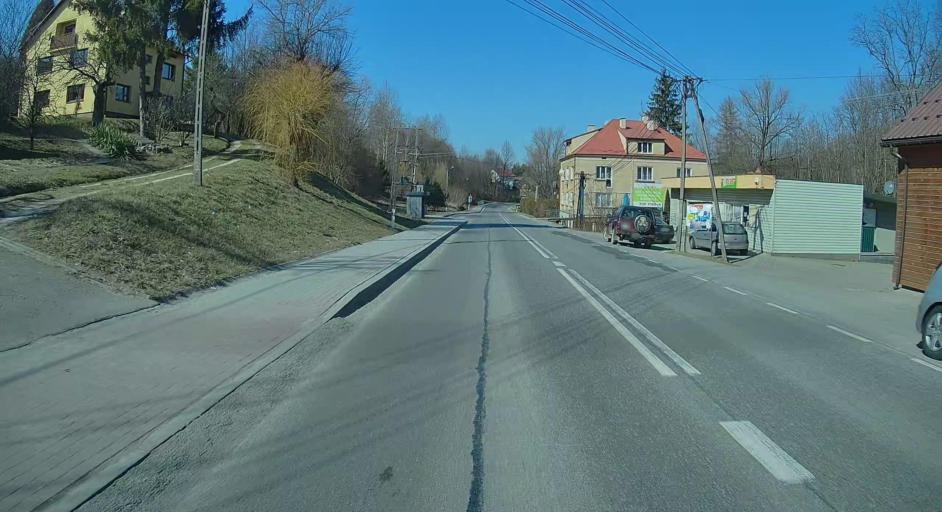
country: PL
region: Subcarpathian Voivodeship
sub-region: Powiat rzeszowski
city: Hyzne
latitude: 49.9052
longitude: 22.2070
